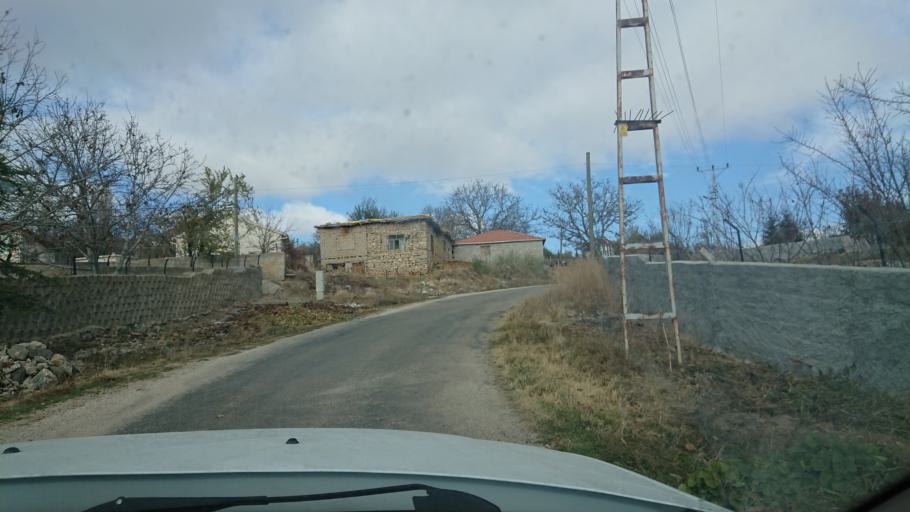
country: TR
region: Aksaray
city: Agacoren
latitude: 38.8218
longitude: 33.9585
